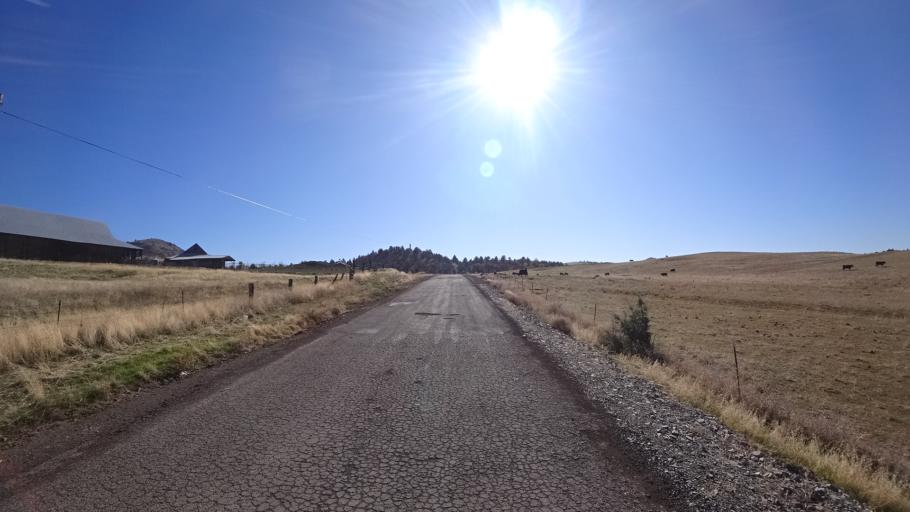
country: US
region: California
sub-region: Siskiyou County
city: Montague
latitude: 41.8125
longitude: -122.3765
